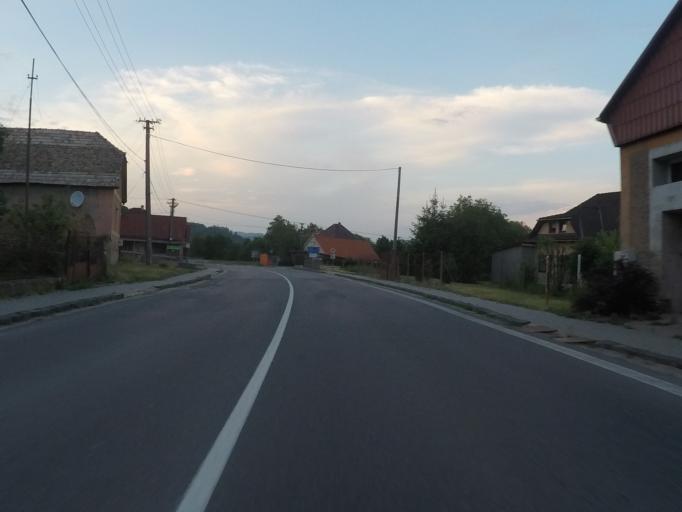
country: SK
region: Banskobystricky
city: Rimavska Sobota
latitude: 48.5120
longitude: 19.9420
